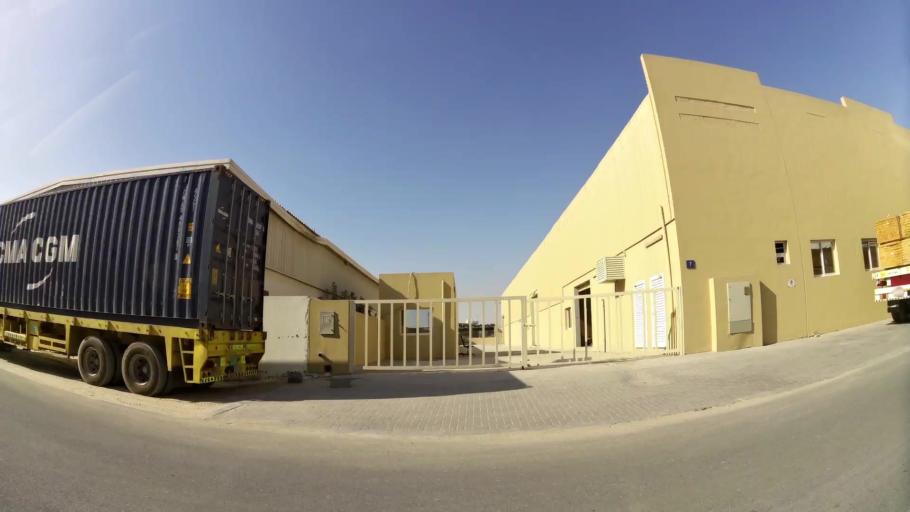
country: AE
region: Dubai
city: Dubai
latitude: 24.9878
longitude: 55.1118
